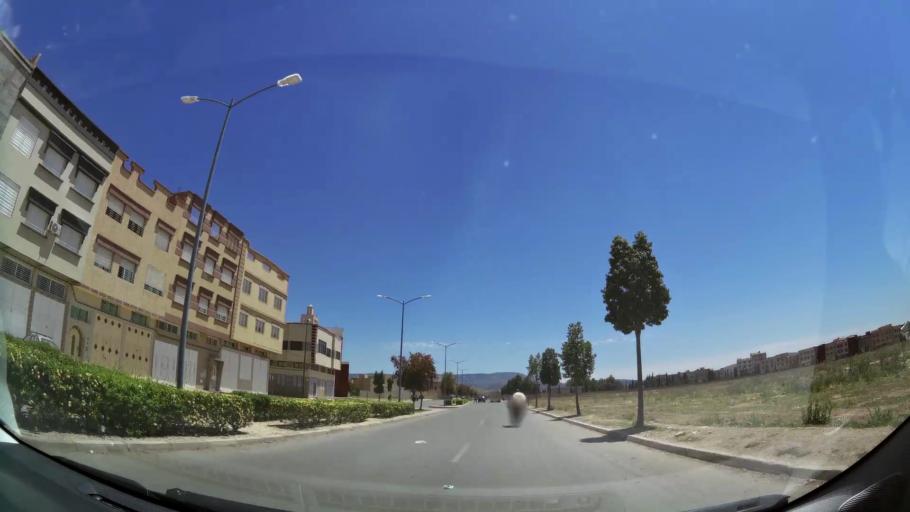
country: MA
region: Oriental
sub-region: Oujda-Angad
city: Oujda
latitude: 34.6790
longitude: -1.8697
